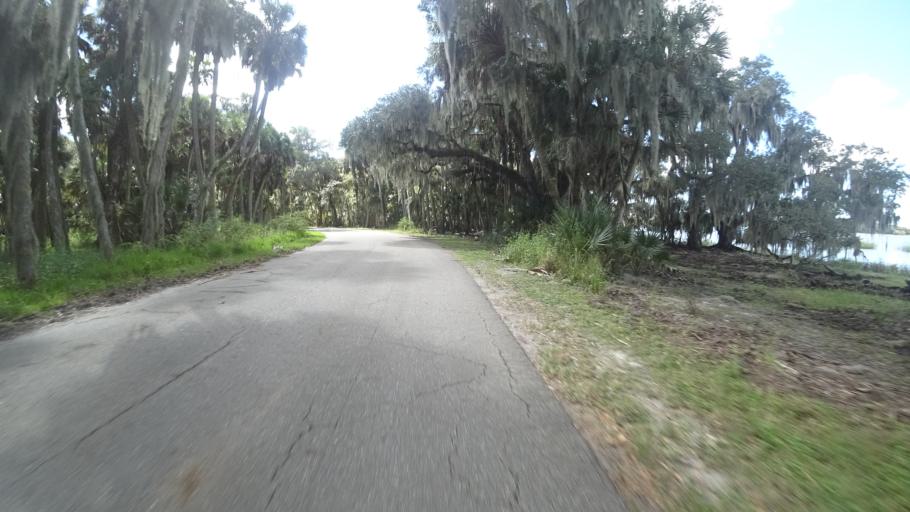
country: US
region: Florida
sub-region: Sarasota County
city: Lake Sarasota
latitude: 27.2664
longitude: -82.2857
